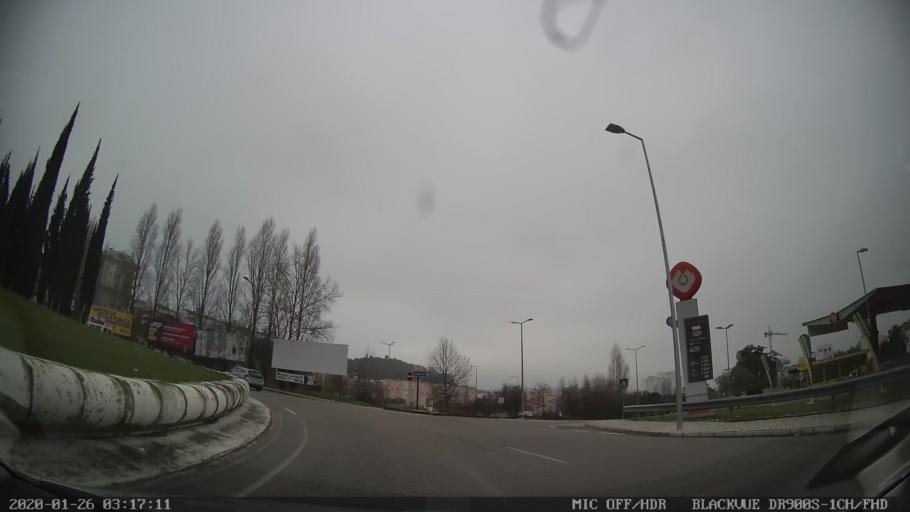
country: PT
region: Santarem
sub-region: Santarem
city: Santarem
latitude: 39.2448
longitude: -8.6905
